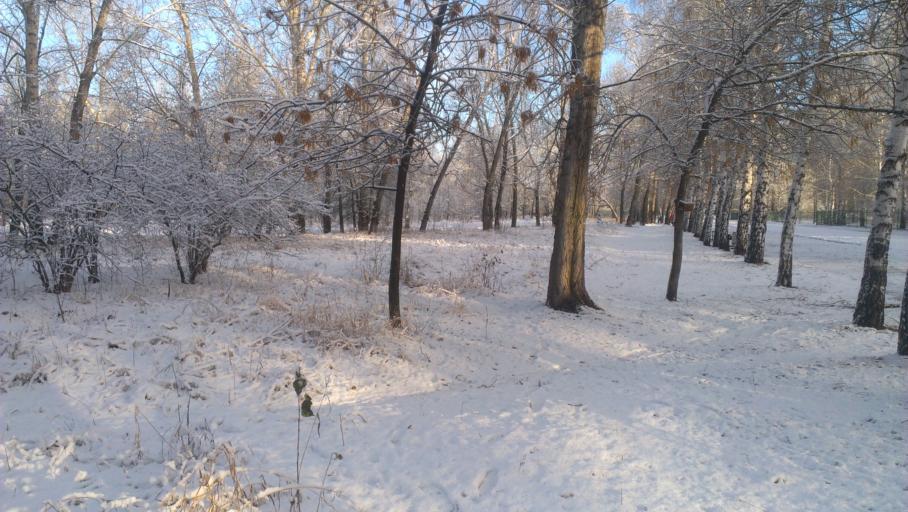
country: RU
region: Altai Krai
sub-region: Gorod Barnaulskiy
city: Barnaul
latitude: 53.3629
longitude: 83.6897
